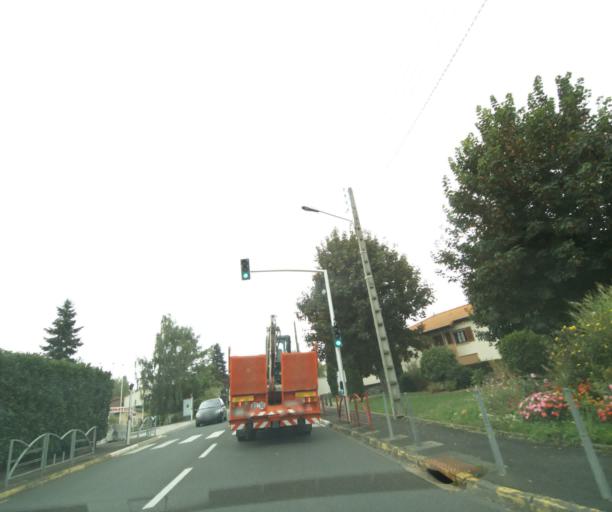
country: FR
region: Auvergne
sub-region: Departement du Puy-de-Dome
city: Ceyrat
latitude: 45.7399
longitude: 3.0596
